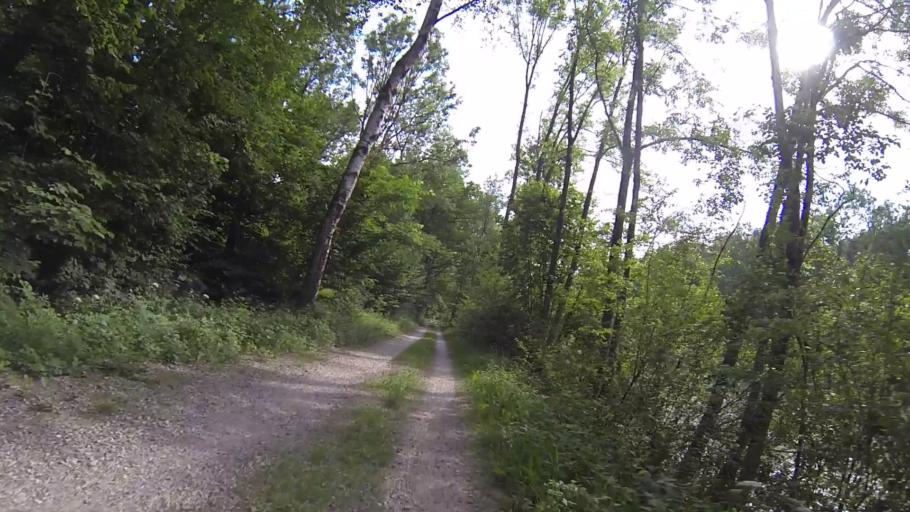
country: DE
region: Bavaria
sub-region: Swabia
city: Neu-Ulm
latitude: 48.3606
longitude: 10.0008
